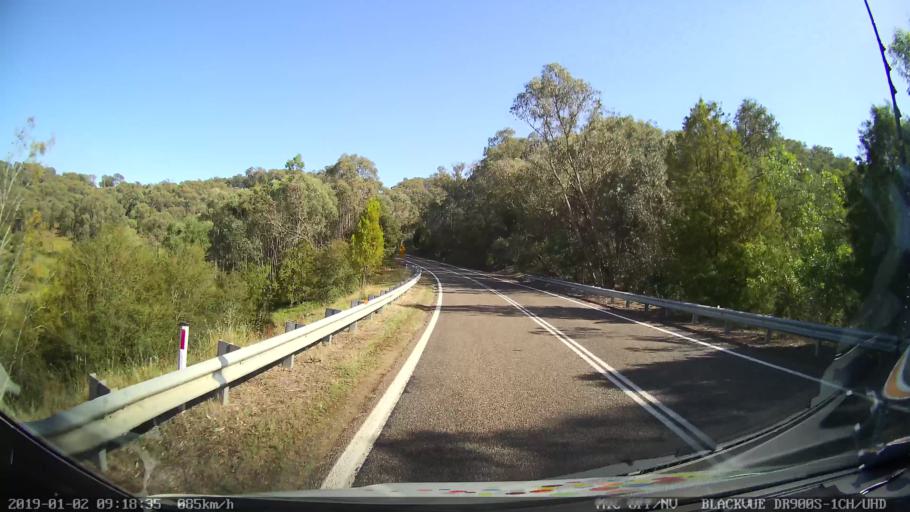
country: AU
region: New South Wales
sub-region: Tumut Shire
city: Tumut
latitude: -35.4272
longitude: 148.2872
